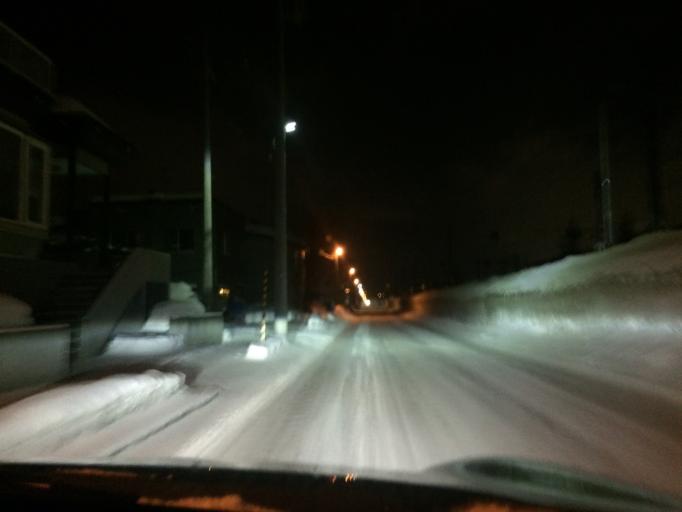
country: JP
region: Hokkaido
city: Sapporo
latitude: 43.0657
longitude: 141.3962
